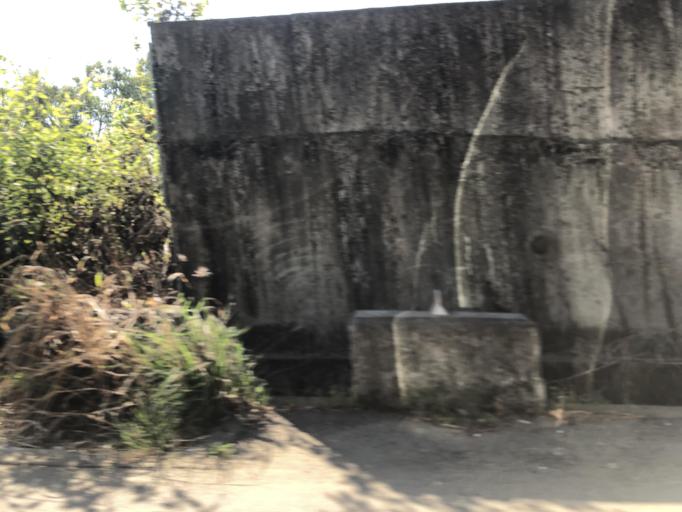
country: TW
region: Taiwan
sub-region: Tainan
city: Tainan
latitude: 23.0375
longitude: 120.3394
